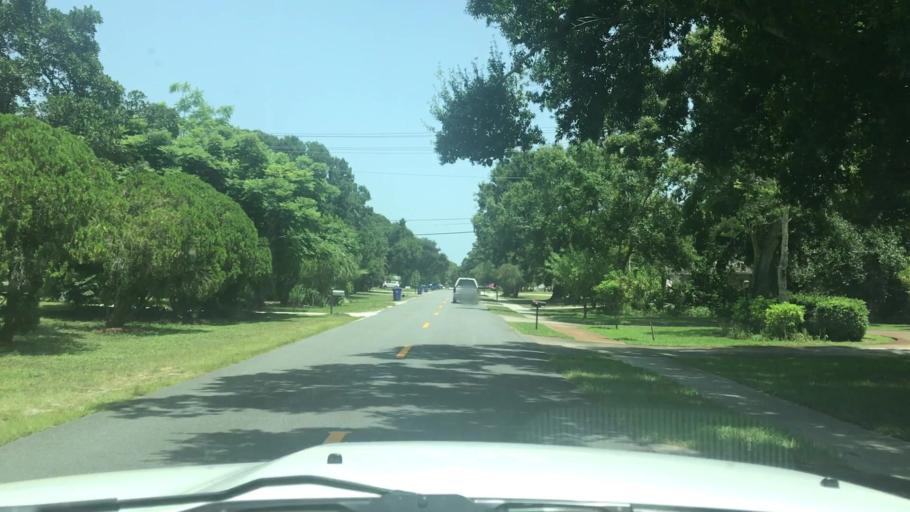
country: US
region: Florida
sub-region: Indian River County
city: Vero Beach
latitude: 27.6426
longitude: -80.4179
